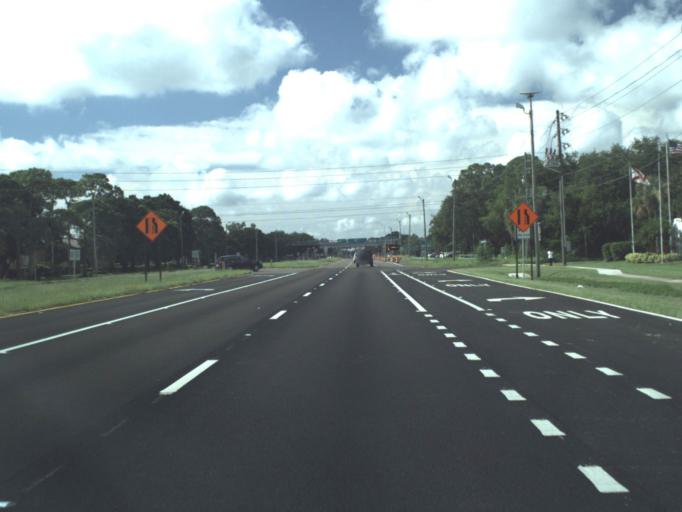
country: US
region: Florida
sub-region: Pinellas County
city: Gandy
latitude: 27.8693
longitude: -82.6389
